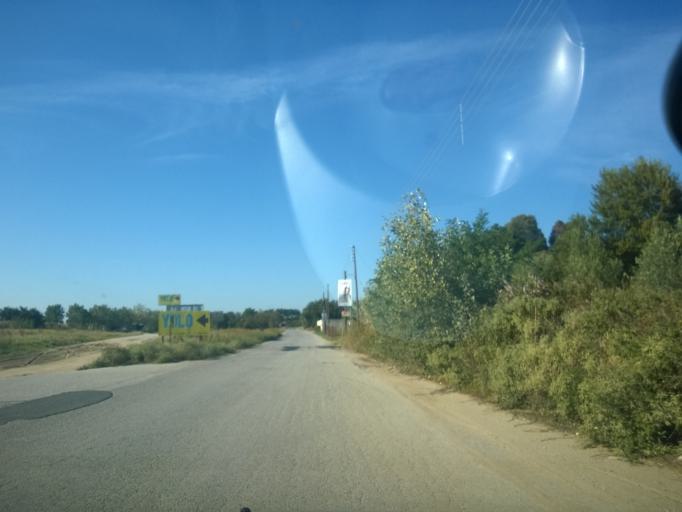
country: GR
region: Central Macedonia
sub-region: Nomos Chalkidikis
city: Nea Kallikrateia
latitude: 40.3325
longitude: 23.0241
